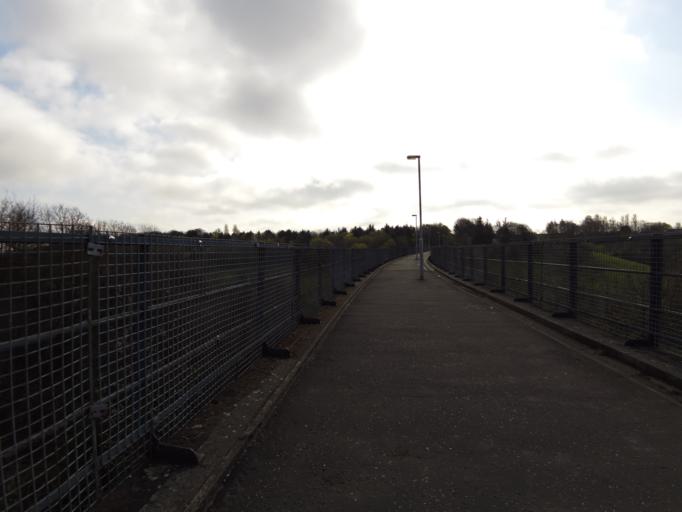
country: GB
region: Scotland
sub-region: Fife
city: Leslie
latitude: 56.1981
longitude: -3.2141
